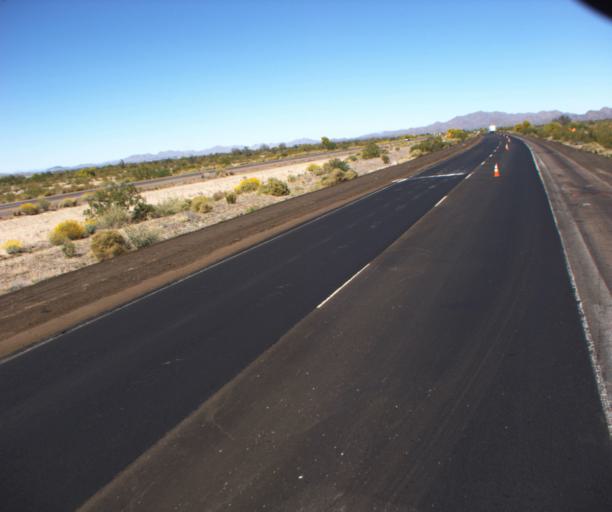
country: US
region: Arizona
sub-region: Maricopa County
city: Gila Bend
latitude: 33.0177
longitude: -112.6508
